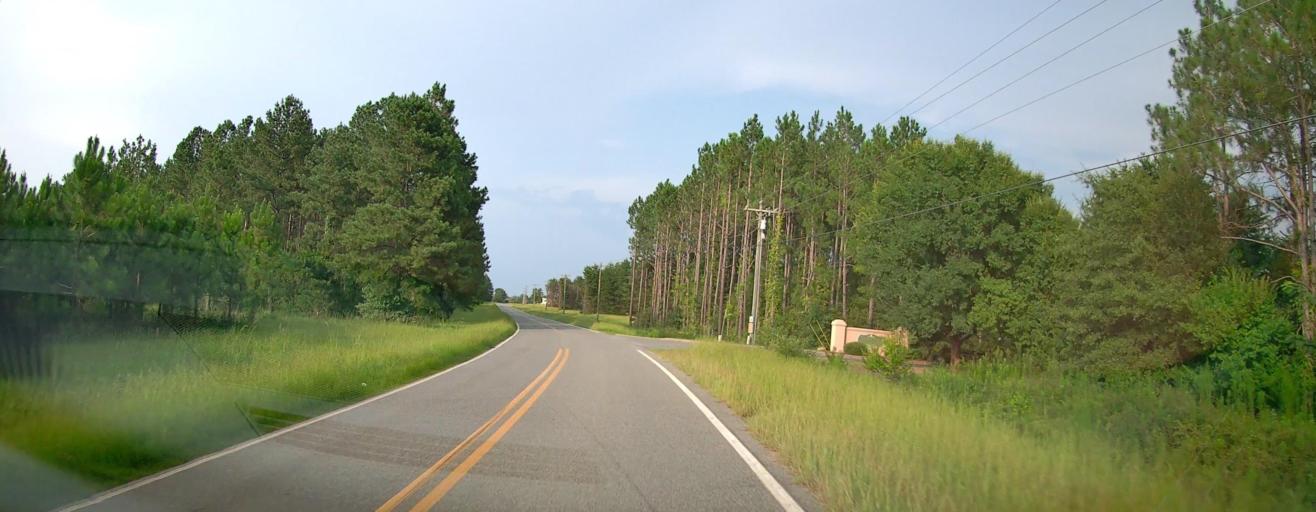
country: US
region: Georgia
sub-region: Laurens County
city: Dublin
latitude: 32.4798
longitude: -82.9520
